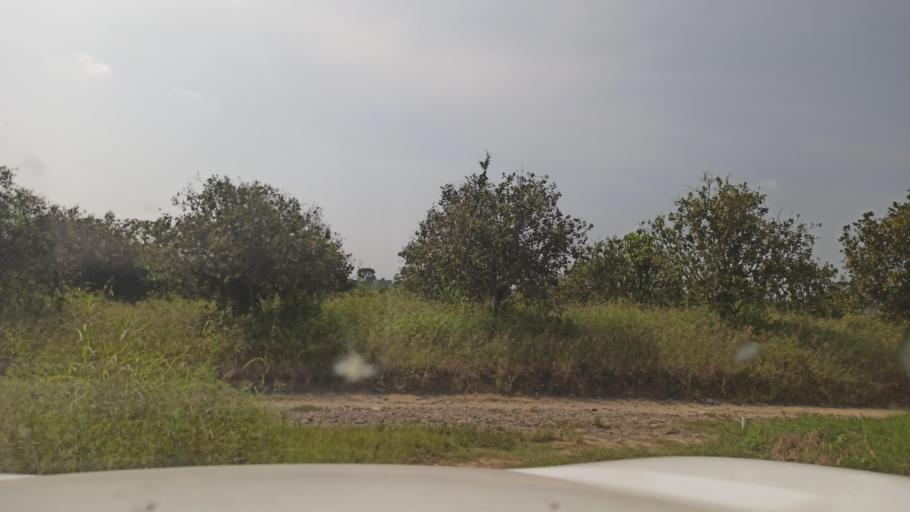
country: MX
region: Veracruz
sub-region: Martinez de la Torre
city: El Progreso
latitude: 20.1468
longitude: -97.0593
